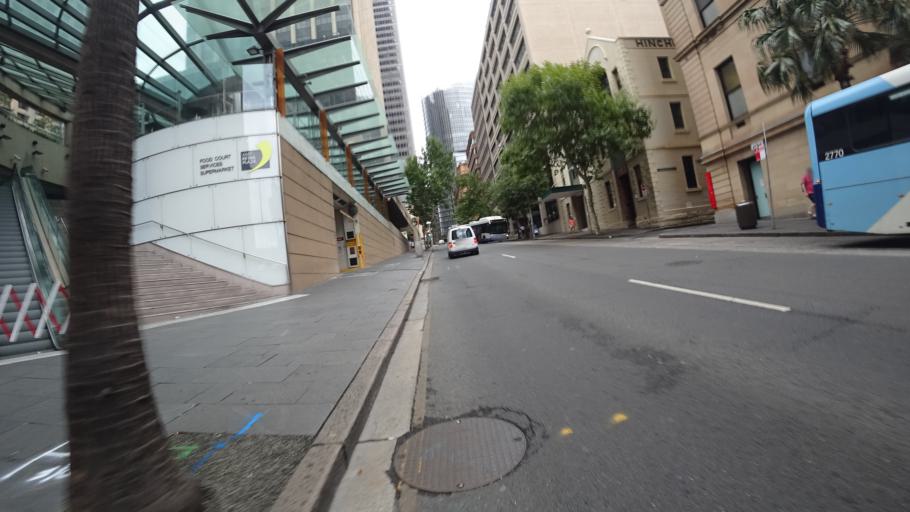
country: AU
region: New South Wales
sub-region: City of Sydney
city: Sydney
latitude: -33.8623
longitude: 151.2112
